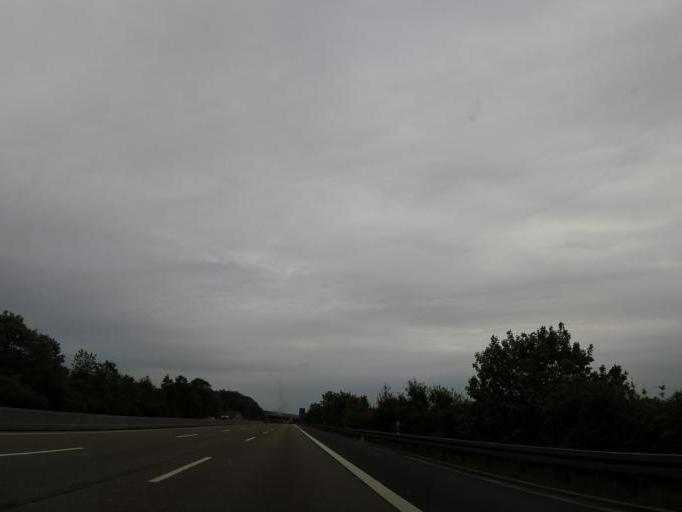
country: DE
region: Hesse
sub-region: Regierungsbezirk Kassel
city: Kirchheim
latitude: 50.8453
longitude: 9.5840
